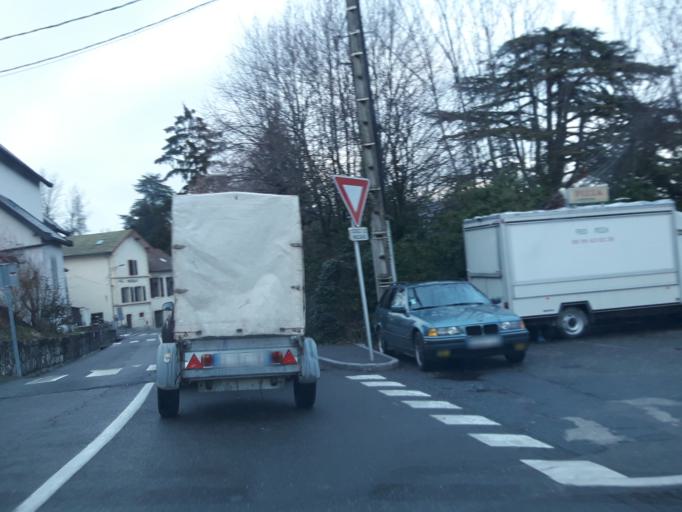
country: FR
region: Rhone-Alpes
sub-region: Departement de la Haute-Savoie
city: Etrembieres
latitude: 46.1623
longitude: 6.2345
